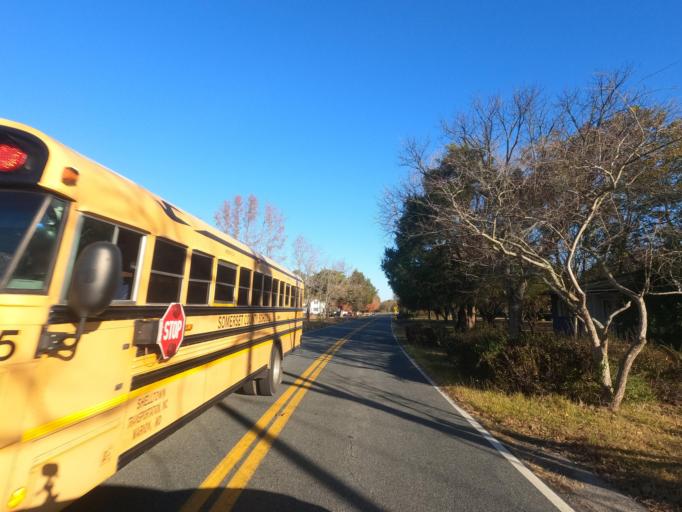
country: US
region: Maryland
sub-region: Somerset County
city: Crisfield
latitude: 38.0110
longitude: -75.8156
